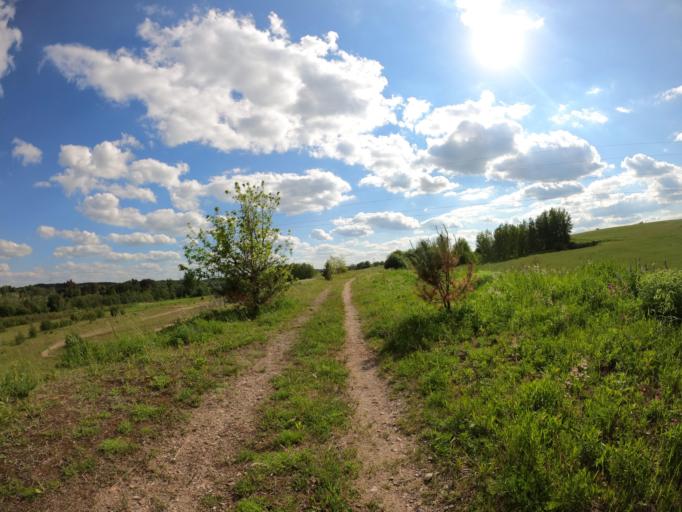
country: PL
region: Warmian-Masurian Voivodeship
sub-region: Powiat lidzbarski
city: Lidzbark Warminski
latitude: 54.1428
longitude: 20.6062
